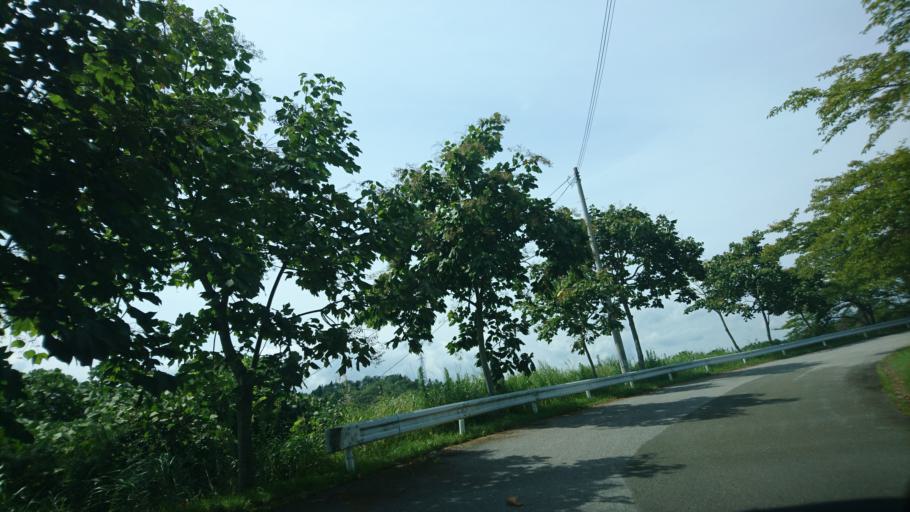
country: JP
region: Iwate
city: Ofunato
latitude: 38.9316
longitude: 141.5950
